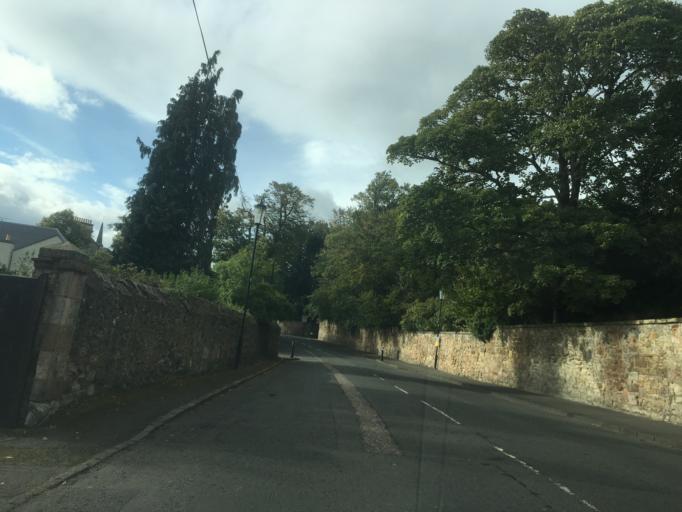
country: GB
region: Scotland
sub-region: East Lothian
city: Musselburgh
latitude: 55.9367
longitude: -3.0459
